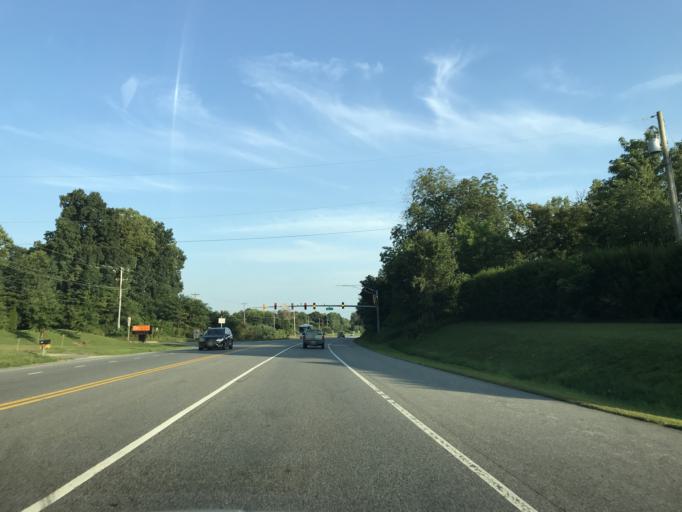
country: US
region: Maryland
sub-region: Cecil County
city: Rising Sun
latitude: 39.6908
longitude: -75.9742
